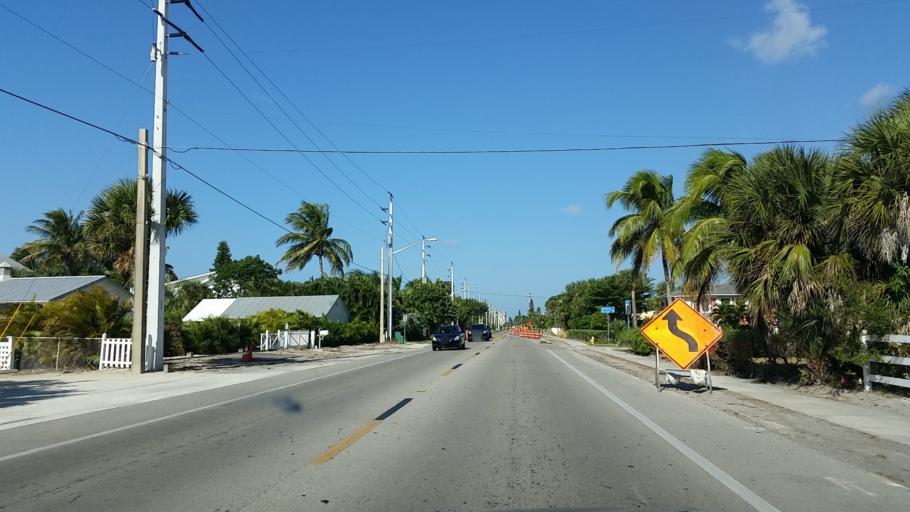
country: US
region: Florida
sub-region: Lee County
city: Fort Myers Beach
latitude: 26.4399
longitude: -81.9261
